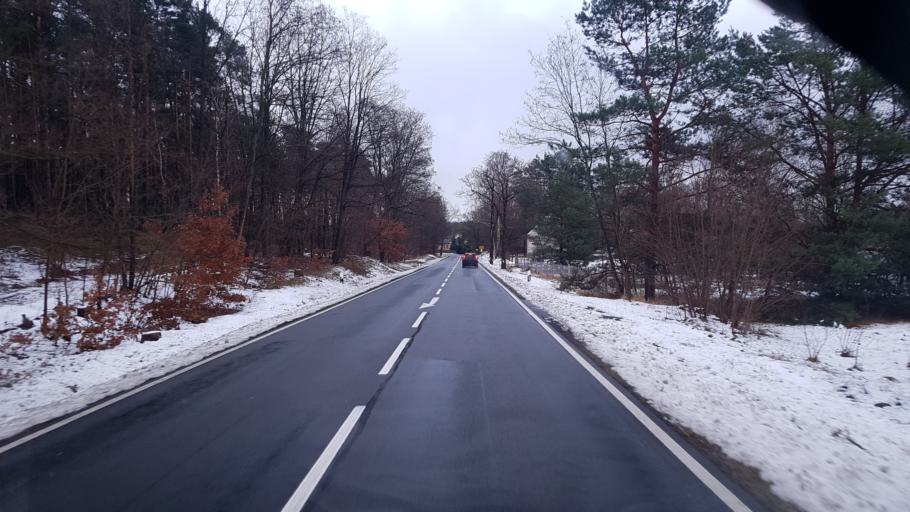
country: DE
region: Brandenburg
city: Jamlitz
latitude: 51.9863
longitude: 14.4046
